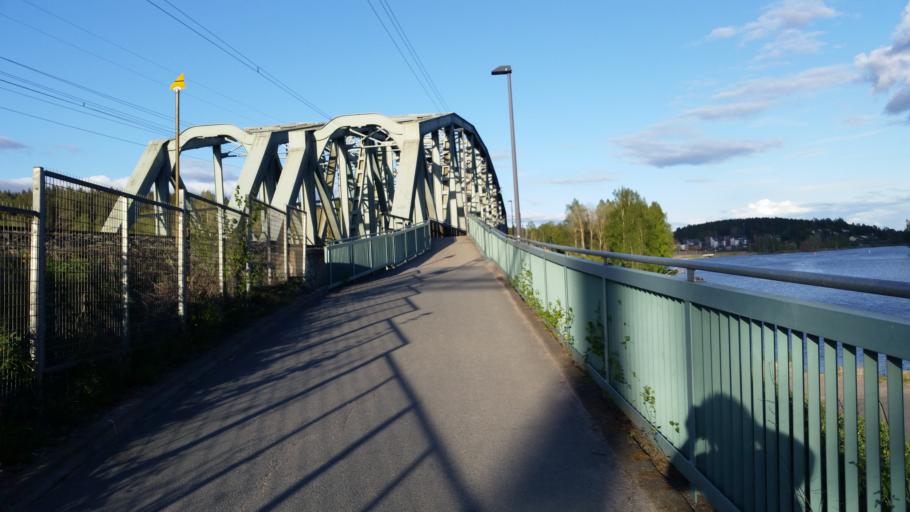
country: FI
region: Haeme
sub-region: Haemeenlinna
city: Haemeenlinna
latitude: 61.0150
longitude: 24.4456
